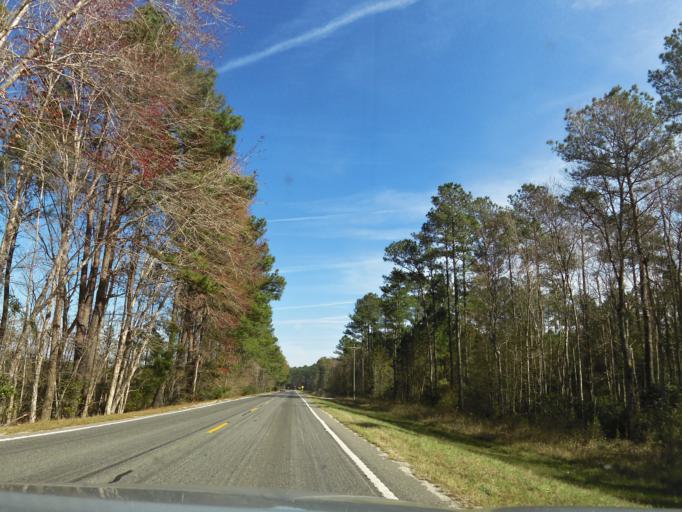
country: US
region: Georgia
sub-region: Glynn County
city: Dock Junction
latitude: 31.2519
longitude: -81.6111
